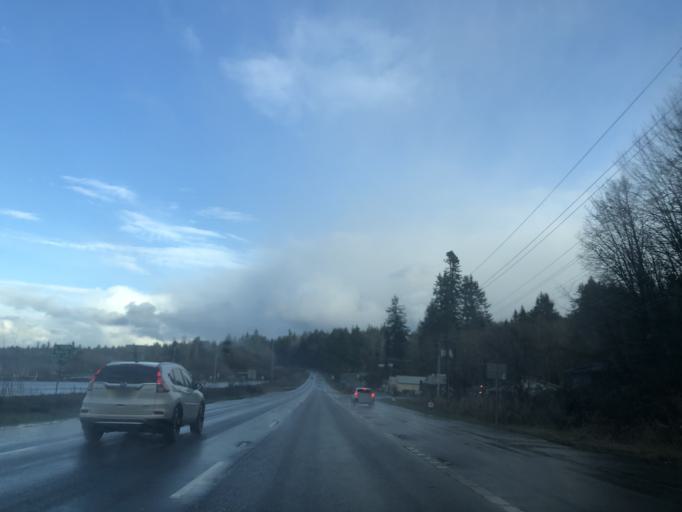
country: US
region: Washington
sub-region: Kitsap County
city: Navy Yard City
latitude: 47.5271
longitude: -122.6841
